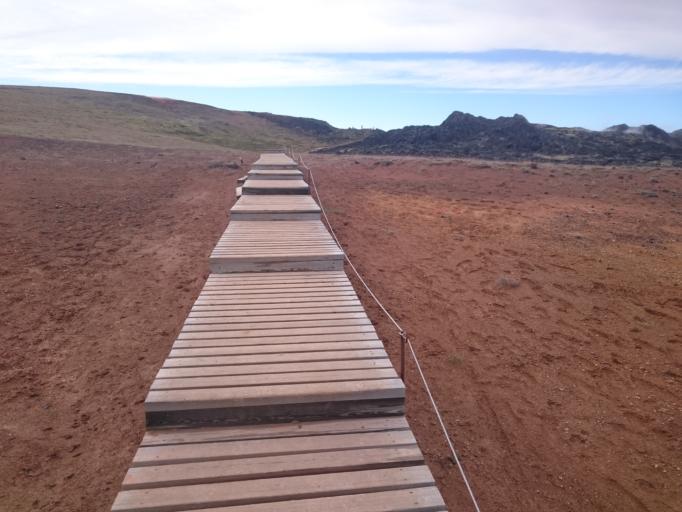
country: IS
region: Northeast
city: Laugar
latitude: 65.7218
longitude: -16.7890
